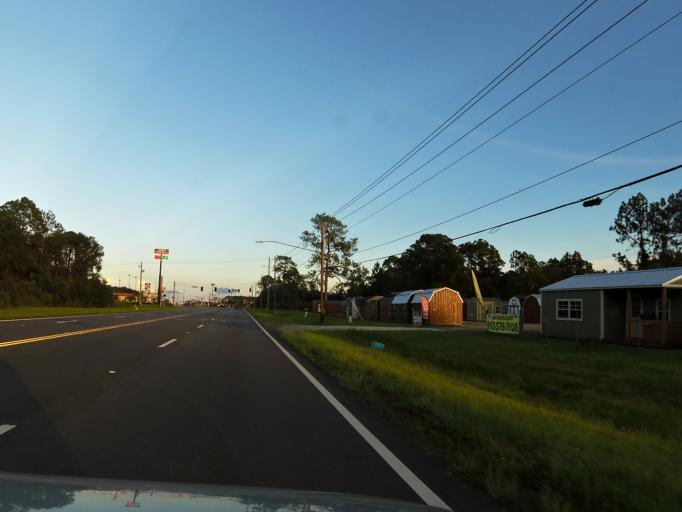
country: US
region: Georgia
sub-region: Camden County
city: Kingsland
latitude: 30.7946
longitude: -81.6694
